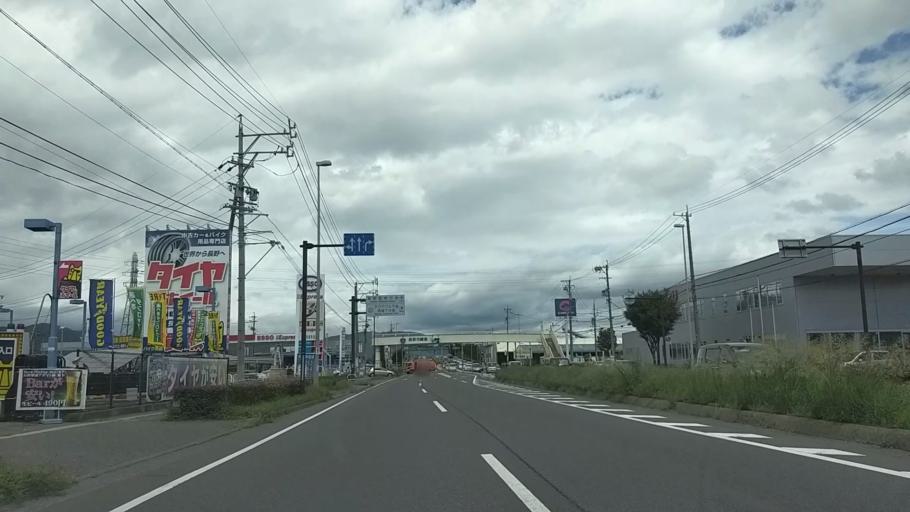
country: JP
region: Nagano
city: Nagano-shi
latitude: 36.6129
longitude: 138.1970
